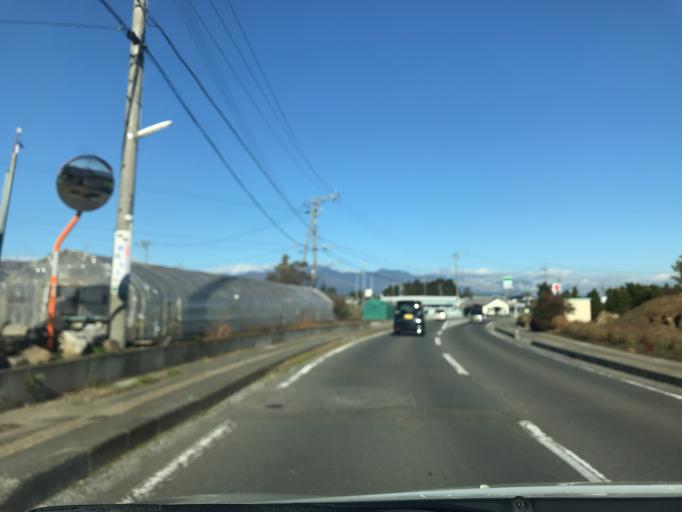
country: JP
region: Nagano
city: Shiojiri
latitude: 36.1280
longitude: 137.9369
